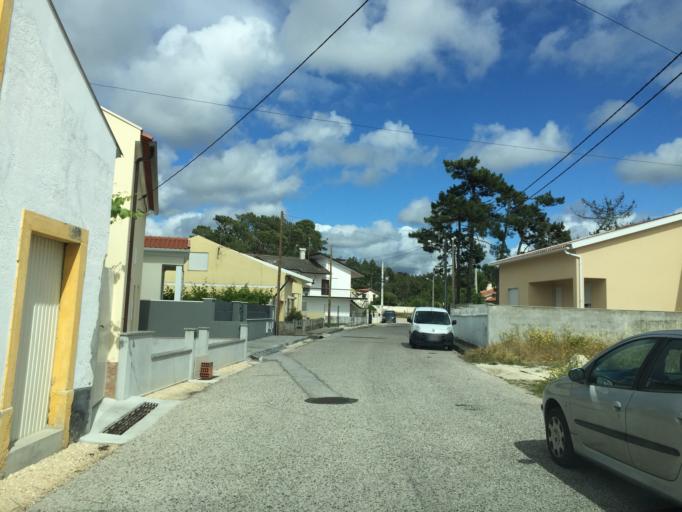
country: PT
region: Coimbra
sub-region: Figueira da Foz
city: Tavarede
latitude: 40.2122
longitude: -8.8444
